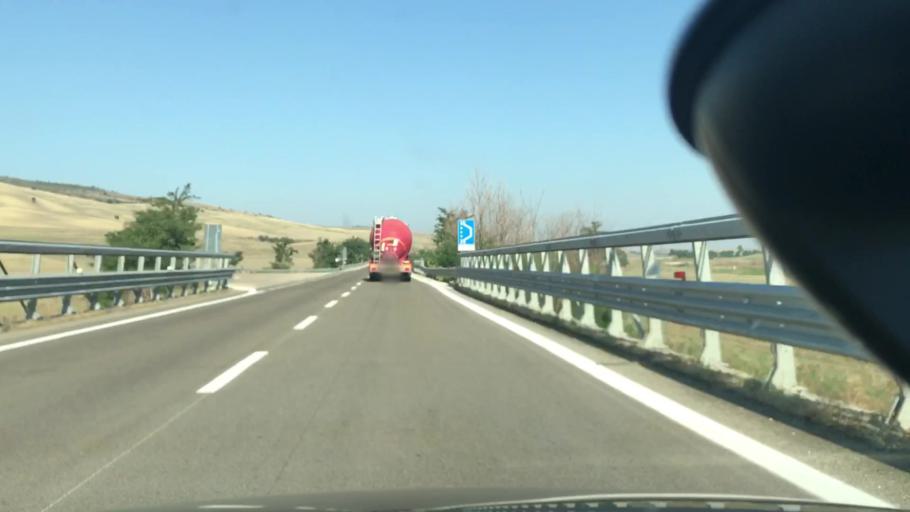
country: IT
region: Basilicate
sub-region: Provincia di Matera
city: Irsina
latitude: 40.7917
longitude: 16.2822
